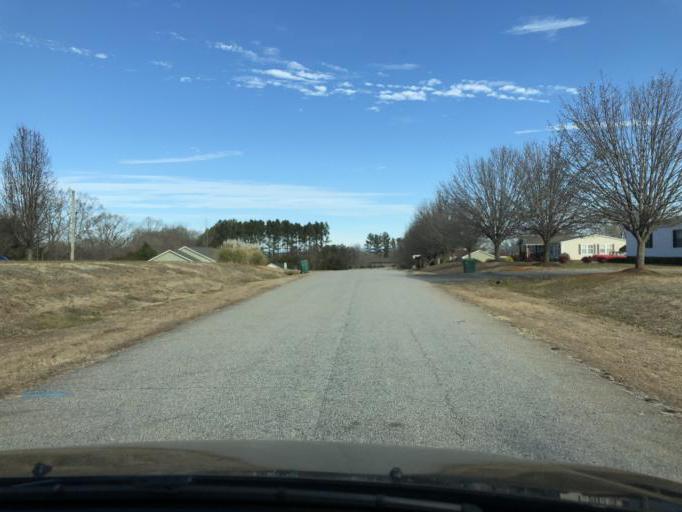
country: US
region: South Carolina
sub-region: Cherokee County
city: East Gaffney
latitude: 35.1397
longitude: -81.6685
